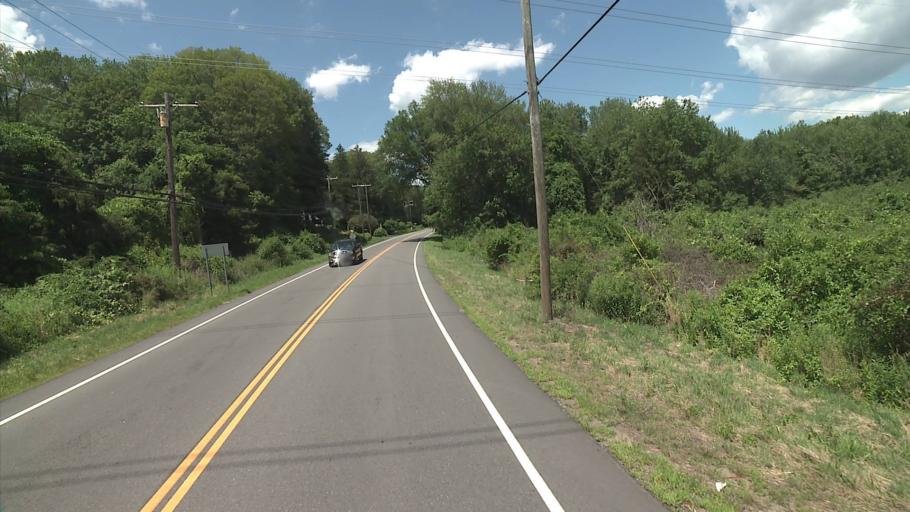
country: US
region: Connecticut
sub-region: Middlesex County
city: East Haddam
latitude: 41.4657
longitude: -72.4446
